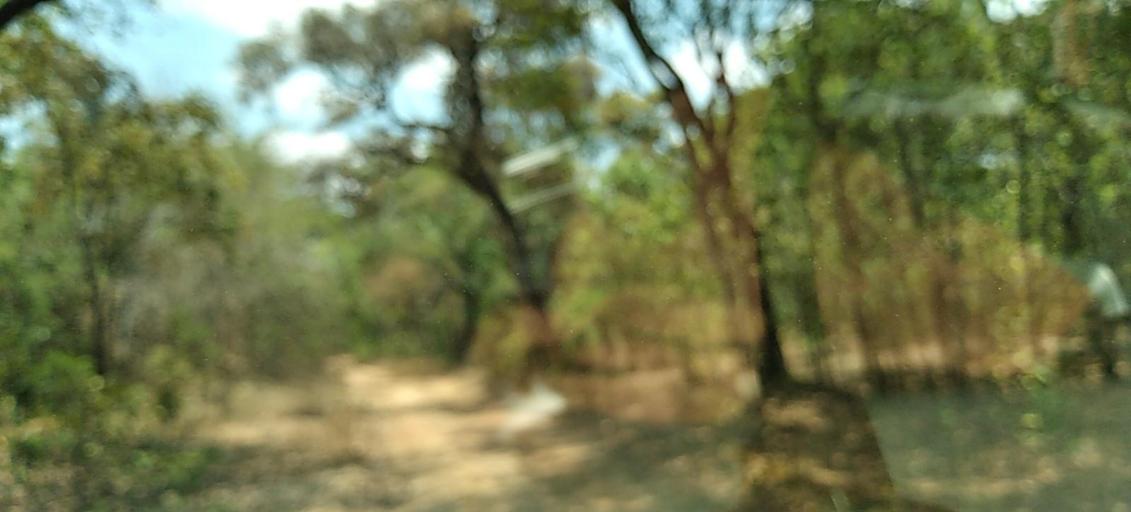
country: ZM
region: Copperbelt
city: Chililabombwe
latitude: -12.4668
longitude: 27.6995
